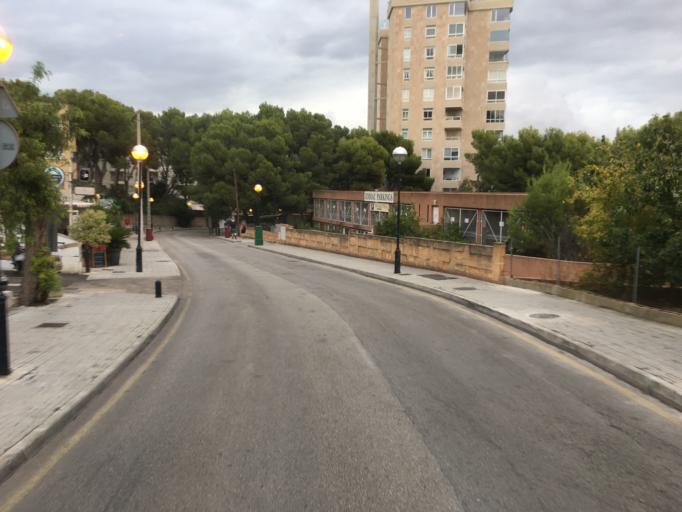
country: ES
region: Balearic Islands
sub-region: Illes Balears
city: Palma
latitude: 39.5416
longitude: 2.5939
